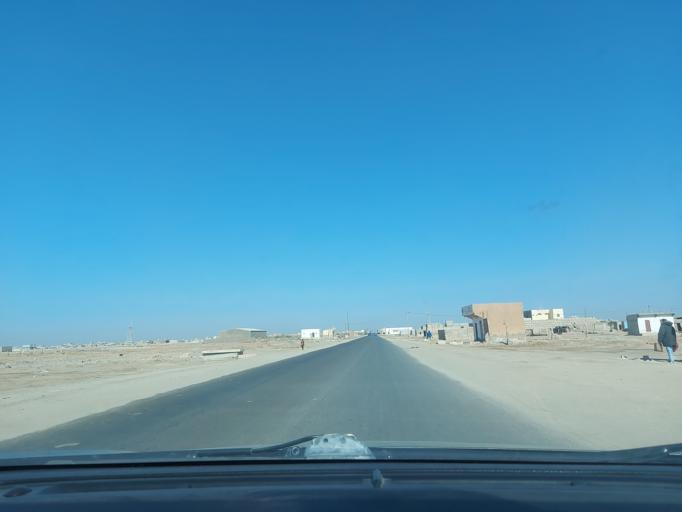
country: MR
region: Nouakchott
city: Nouakchott
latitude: 18.0108
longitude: -15.9813
